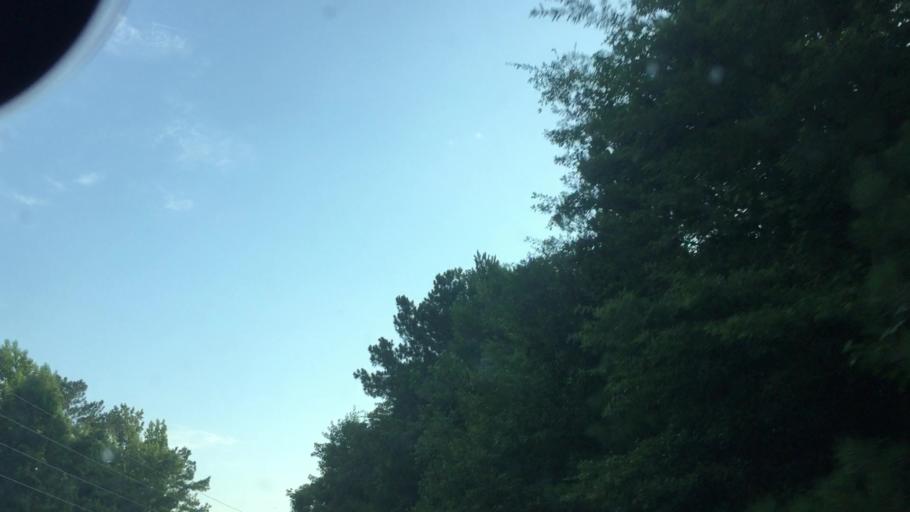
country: US
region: Georgia
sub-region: Henry County
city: Stockbridge
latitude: 33.5572
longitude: -84.1374
